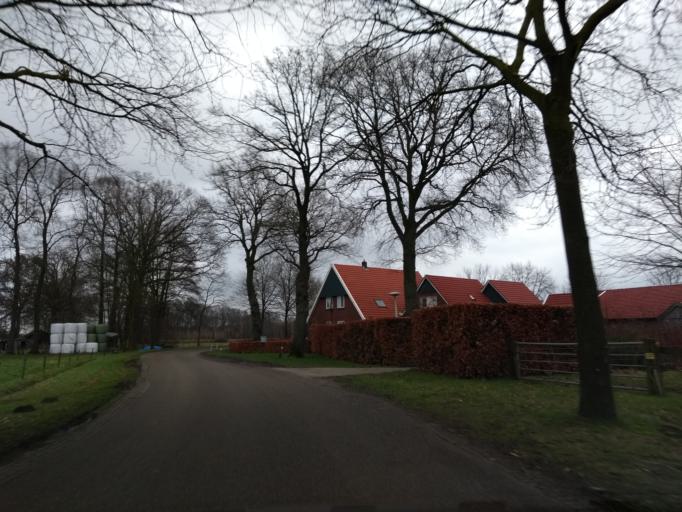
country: NL
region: Overijssel
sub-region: Gemeente Haaksbergen
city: Haaksbergen
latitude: 52.1444
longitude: 6.7527
